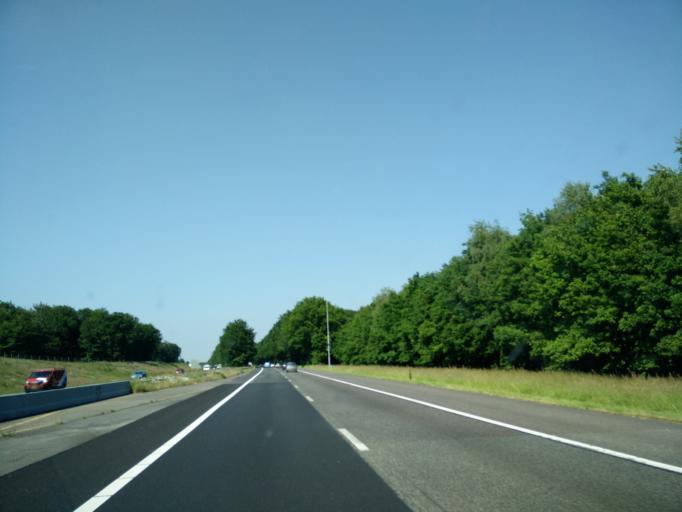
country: NL
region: Drenthe
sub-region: Gemeente Hoogeveen
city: Hoogeveen
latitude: 52.8200
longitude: 6.4666
